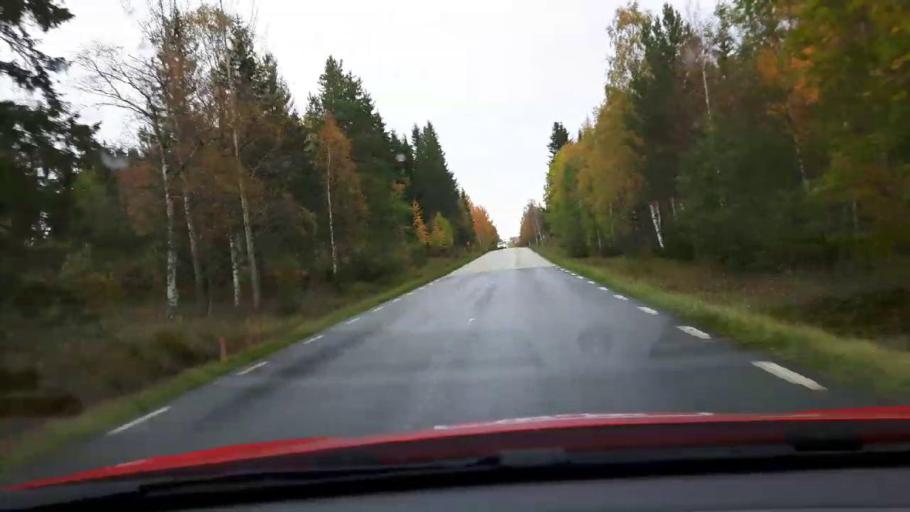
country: SE
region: Jaemtland
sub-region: Bergs Kommun
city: Hoverberg
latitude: 62.9913
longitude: 14.3392
